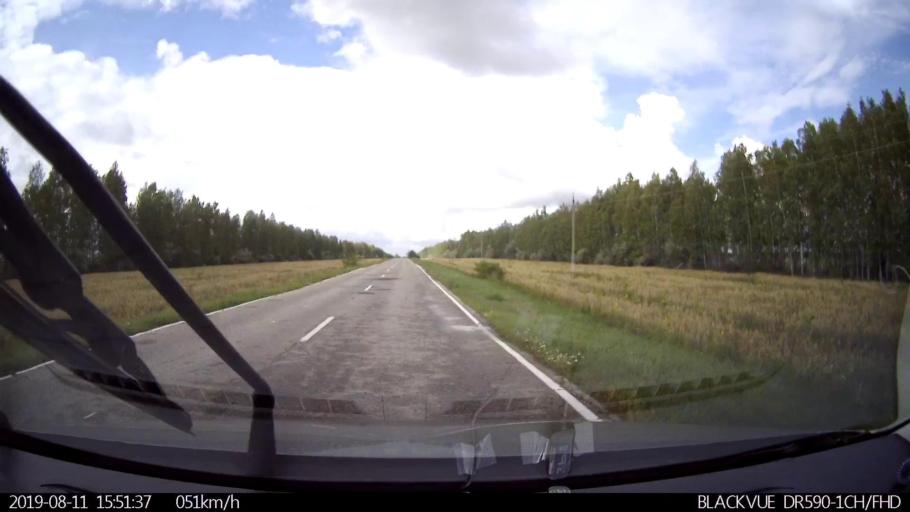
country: RU
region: Ulyanovsk
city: Ignatovka
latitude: 53.9201
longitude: 47.6561
